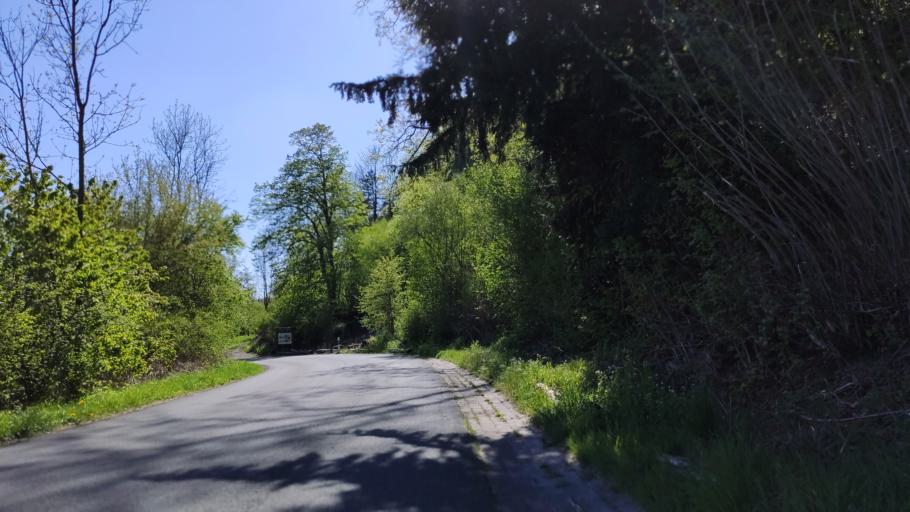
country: DE
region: Lower Saxony
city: Boffzen
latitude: 51.7566
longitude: 9.3693
